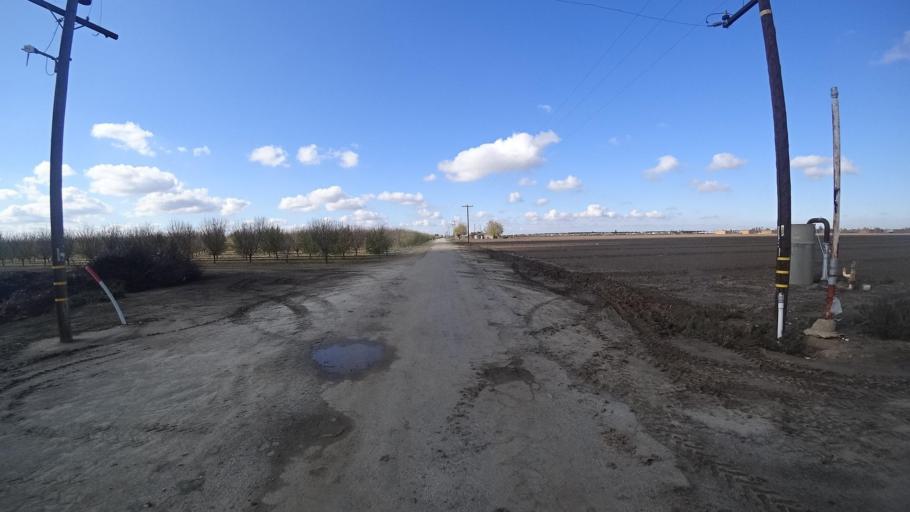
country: US
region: California
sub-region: Kern County
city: McFarland
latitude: 35.6600
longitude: -119.2136
